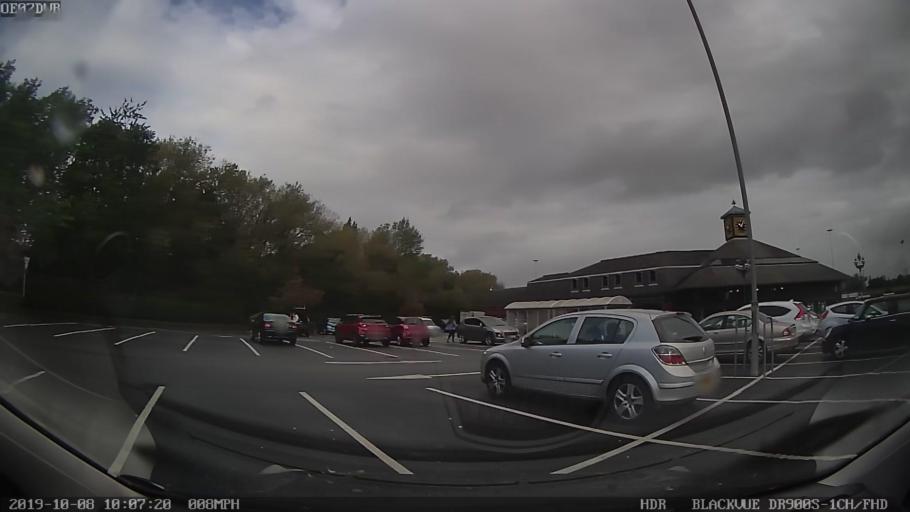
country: GB
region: England
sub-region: Manchester
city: Failsworth
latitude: 53.5209
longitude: -2.1542
